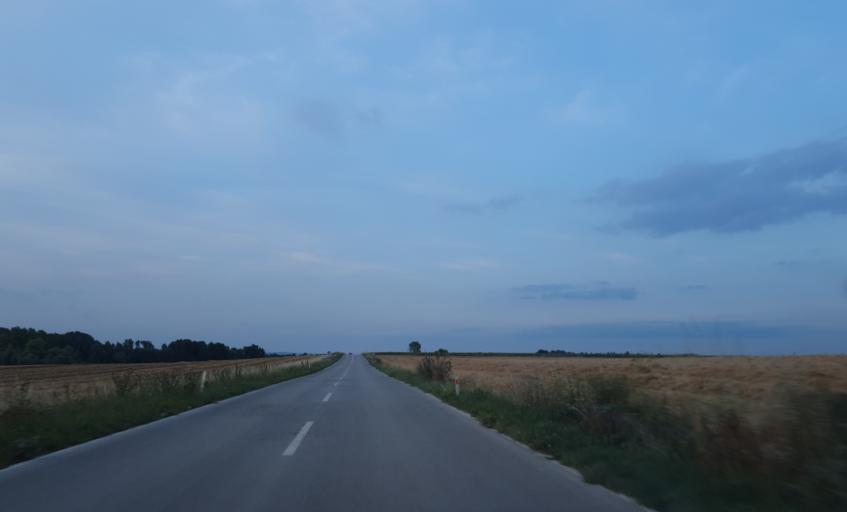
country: TR
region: Tekirdag
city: Beyazkoy
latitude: 41.3999
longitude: 27.6380
